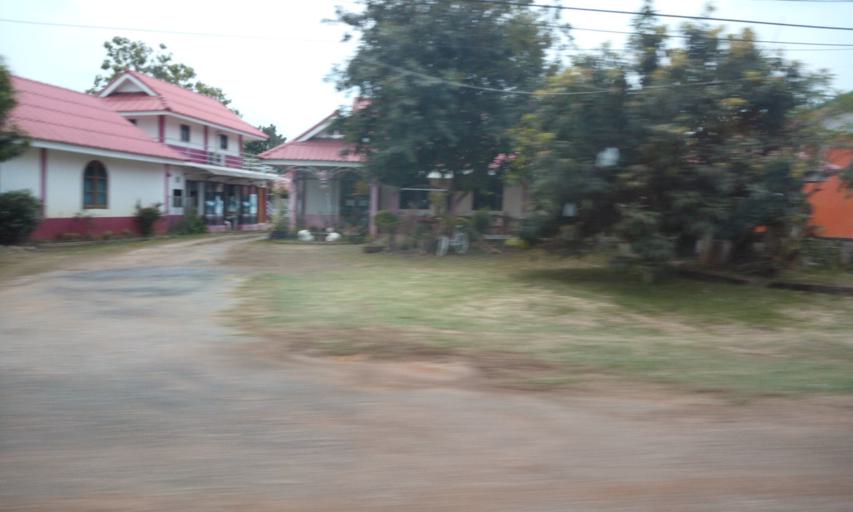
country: TH
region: Phayao
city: Chiang Kham
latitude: 19.5139
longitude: 100.3160
